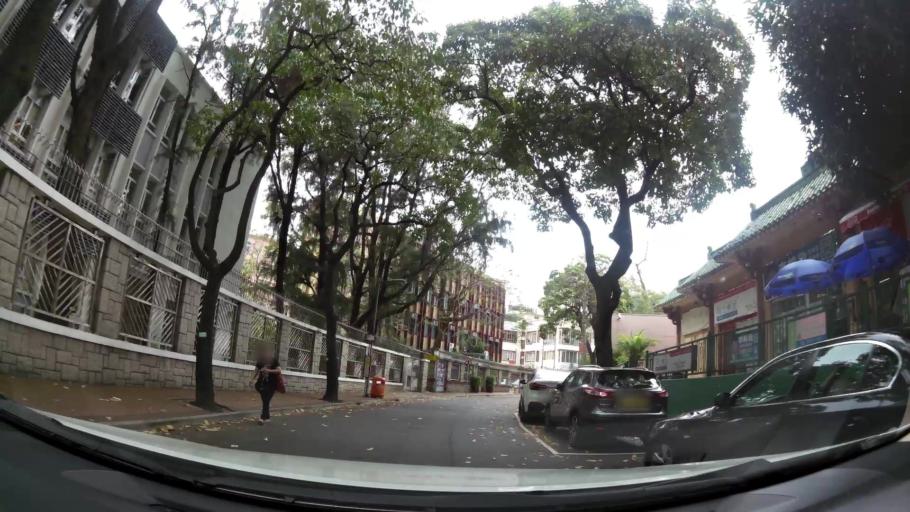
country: HK
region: Sham Shui Po
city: Sham Shui Po
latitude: 22.3311
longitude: 114.1727
